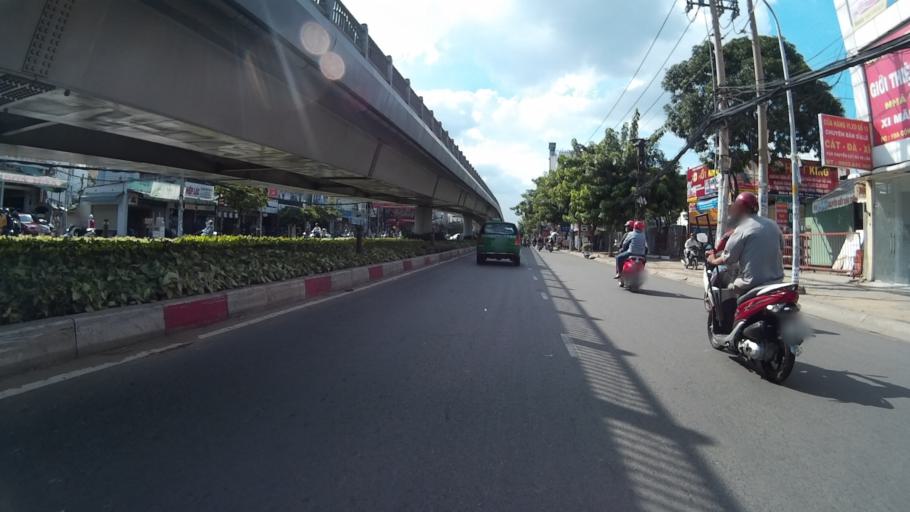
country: VN
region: Ho Chi Minh City
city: Quan Tan Phu
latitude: 10.8020
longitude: 106.6483
